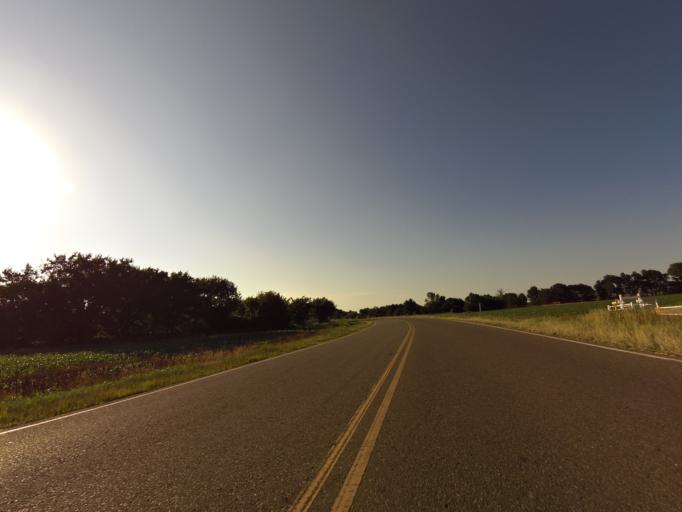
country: US
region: Kansas
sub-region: Reno County
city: Buhler
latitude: 38.1465
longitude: -97.8296
